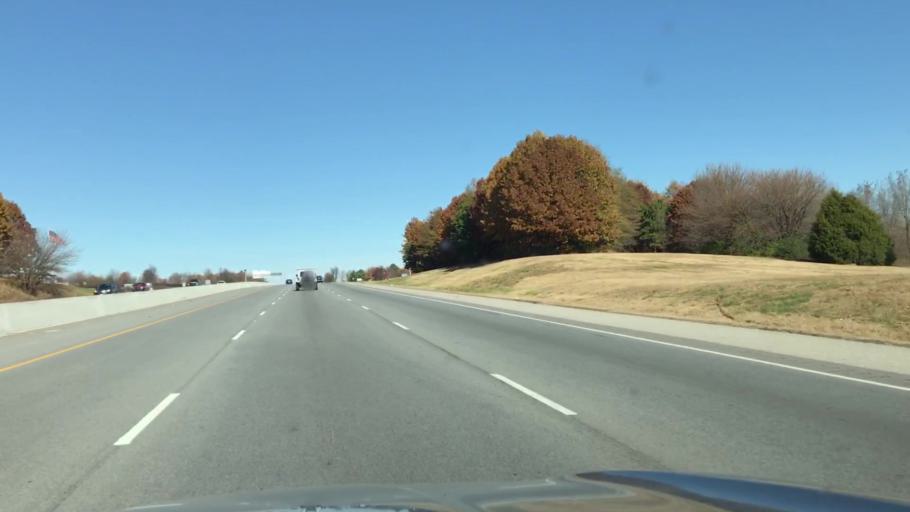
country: US
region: Arkansas
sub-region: Benton County
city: Lowell
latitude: 36.2547
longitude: -94.1503
